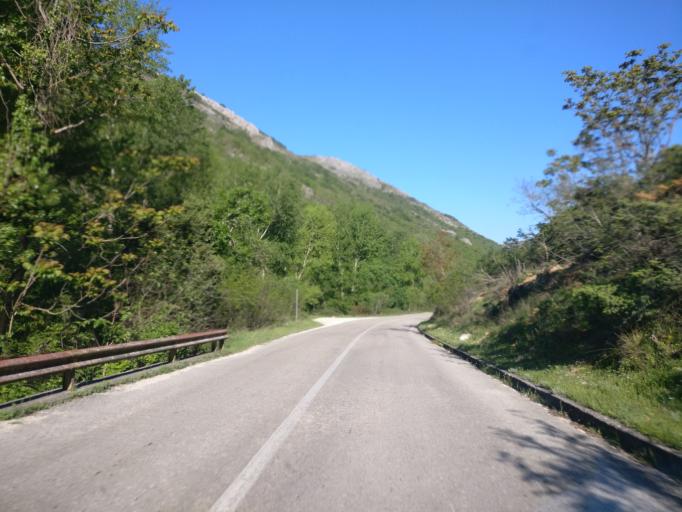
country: BA
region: Federation of Bosnia and Herzegovina
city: Stolac
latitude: 43.0869
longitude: 18.0029
